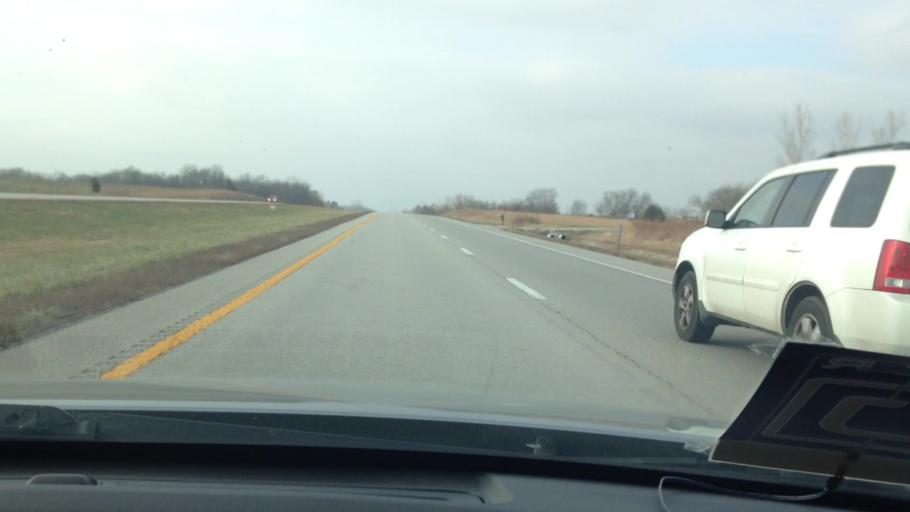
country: US
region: Missouri
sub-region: Cass County
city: Garden City
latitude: 38.5305
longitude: -94.1502
